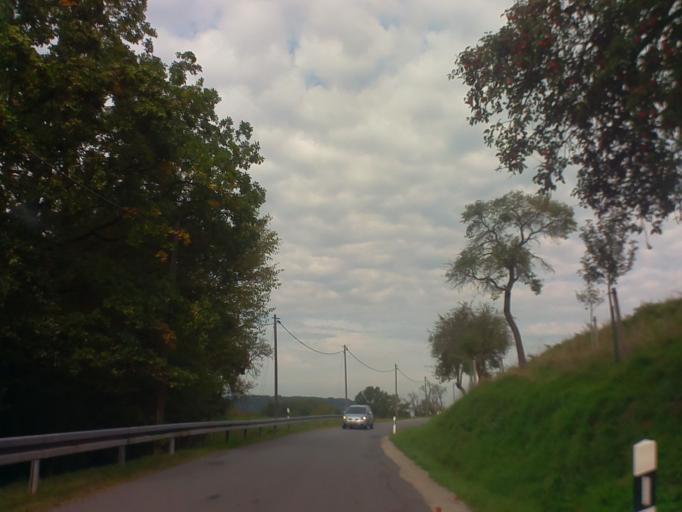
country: DE
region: Thuringia
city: Schops
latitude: 50.8276
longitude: 11.6055
